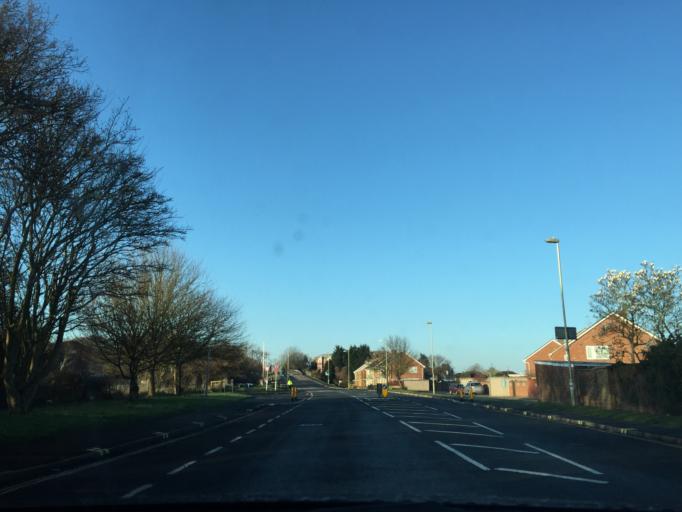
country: GB
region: England
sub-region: Hampshire
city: Fareham
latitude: 50.8211
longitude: -1.1643
